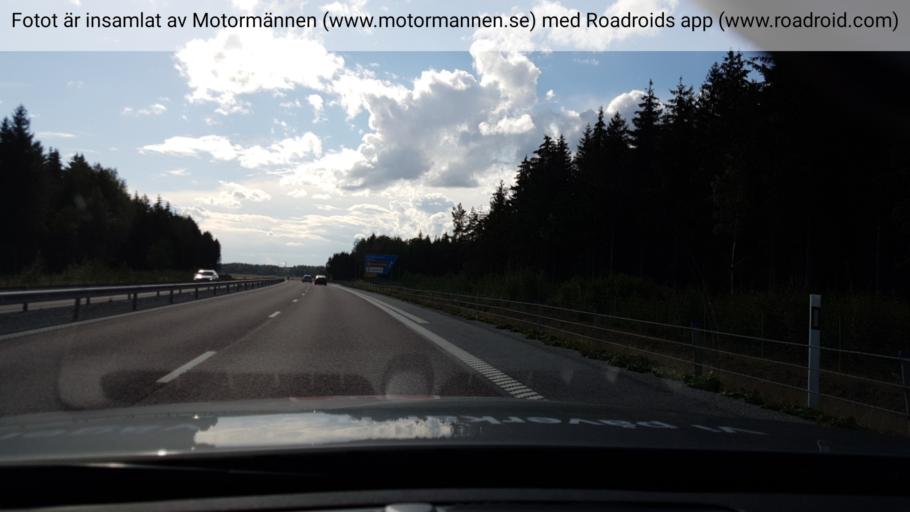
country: SE
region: Vaestmanland
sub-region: Vasteras
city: Tillberga
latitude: 59.6239
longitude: 16.6748
